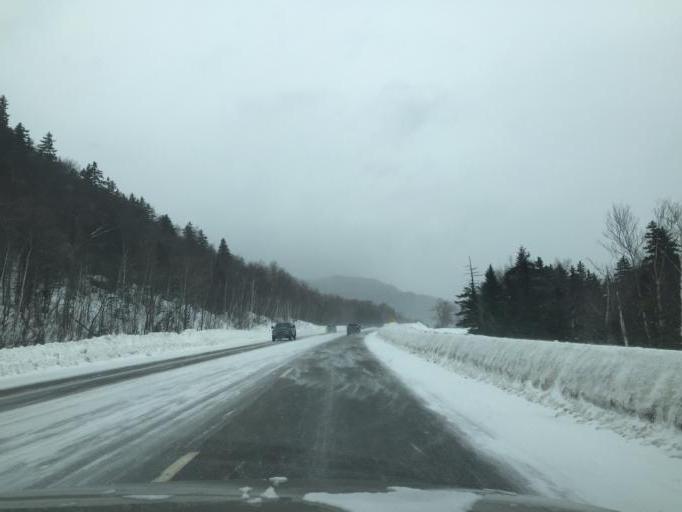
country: US
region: New Hampshire
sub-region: Coos County
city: Gorham
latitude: 44.2484
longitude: -71.2536
